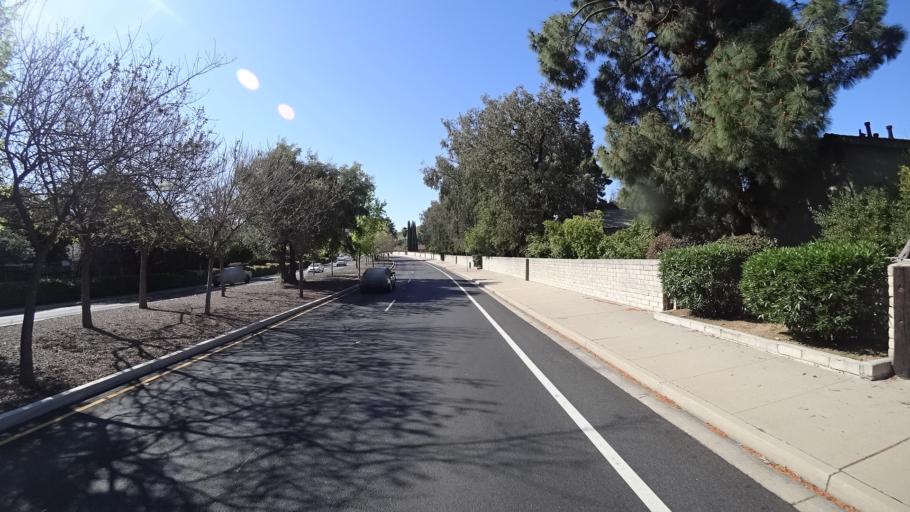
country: US
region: California
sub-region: Ventura County
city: Casa Conejo
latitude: 34.2154
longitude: -118.8880
